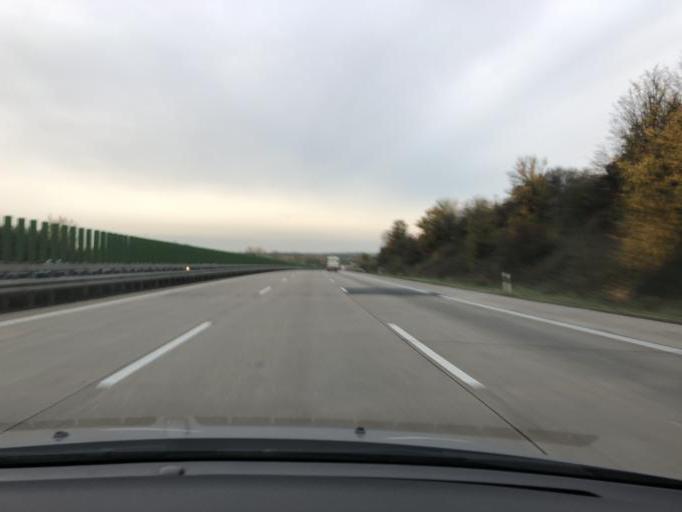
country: DE
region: Saxony-Anhalt
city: Osterfeld
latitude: 51.0714
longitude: 11.9549
